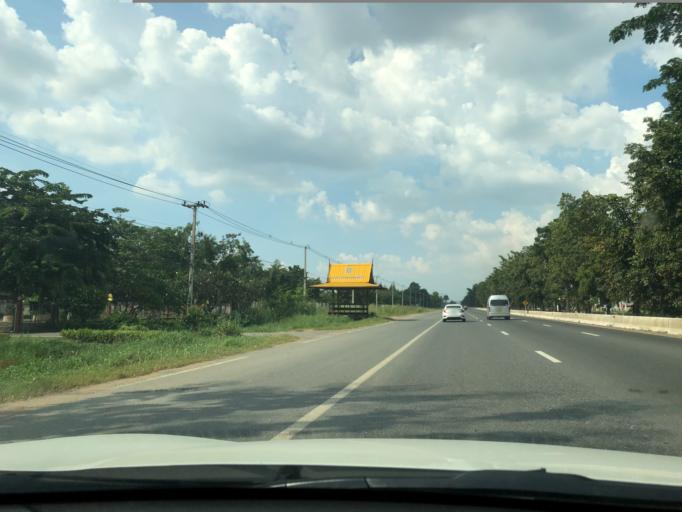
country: TH
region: Nakhon Sawan
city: Krok Phra
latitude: 15.5792
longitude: 100.1246
